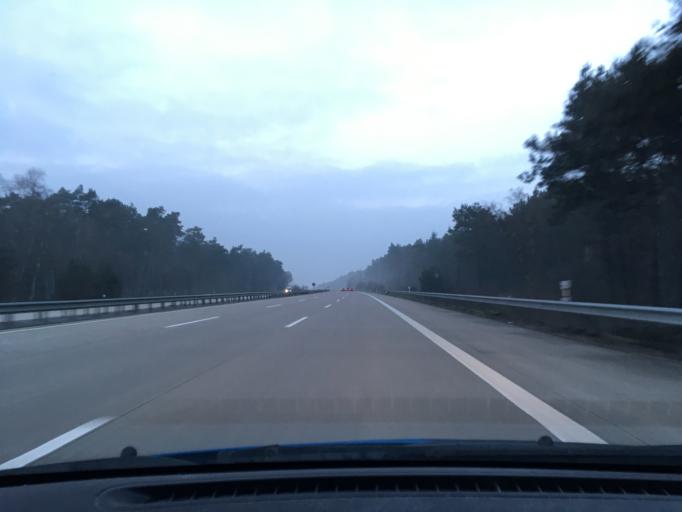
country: DE
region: Lower Saxony
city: Egestorf
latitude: 53.1667
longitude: 10.0710
